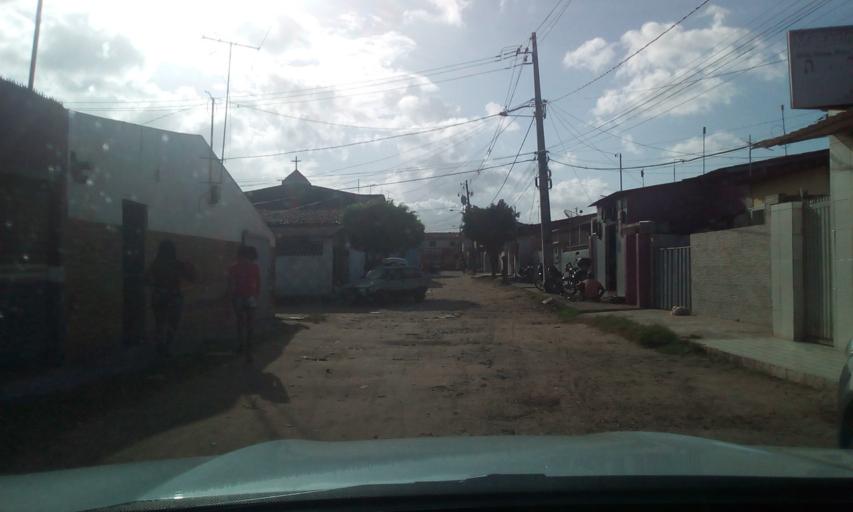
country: BR
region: Paraiba
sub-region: Joao Pessoa
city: Joao Pessoa
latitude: -7.1861
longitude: -34.8817
